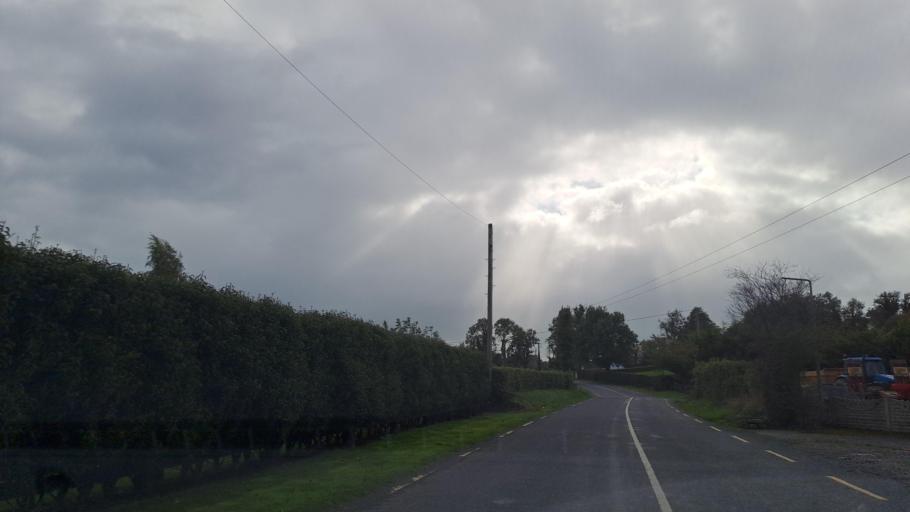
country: IE
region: Ulster
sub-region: County Monaghan
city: Carrickmacross
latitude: 54.0222
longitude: -6.7110
